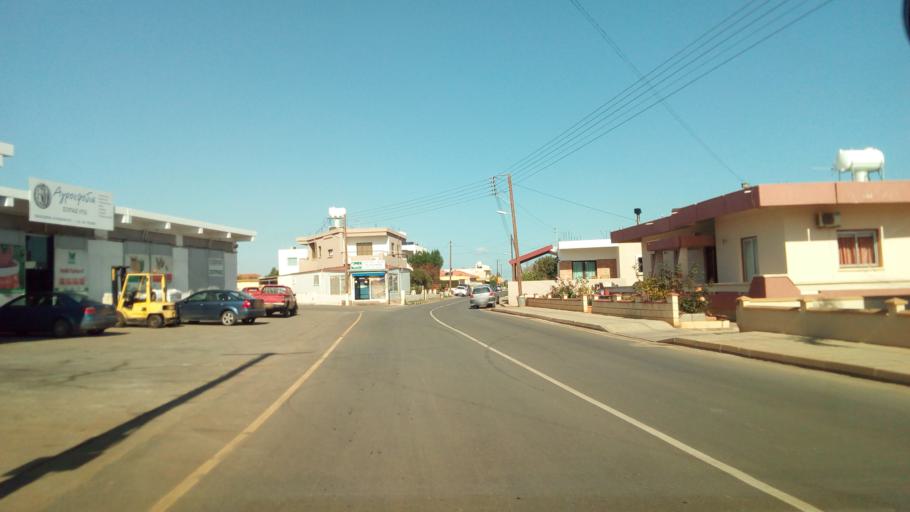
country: CY
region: Ammochostos
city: Liopetri
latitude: 34.9809
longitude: 33.8491
